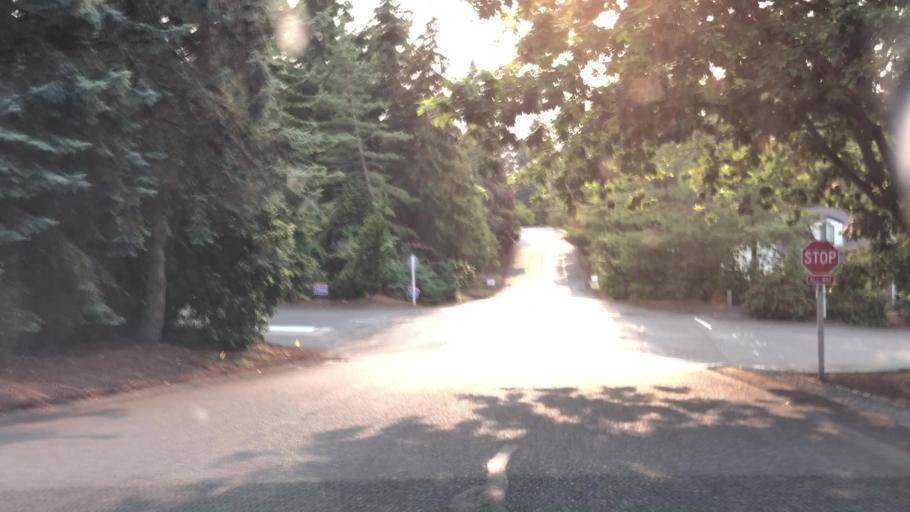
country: US
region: Washington
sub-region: King County
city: Mercer Island
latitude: 47.5411
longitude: -122.2305
